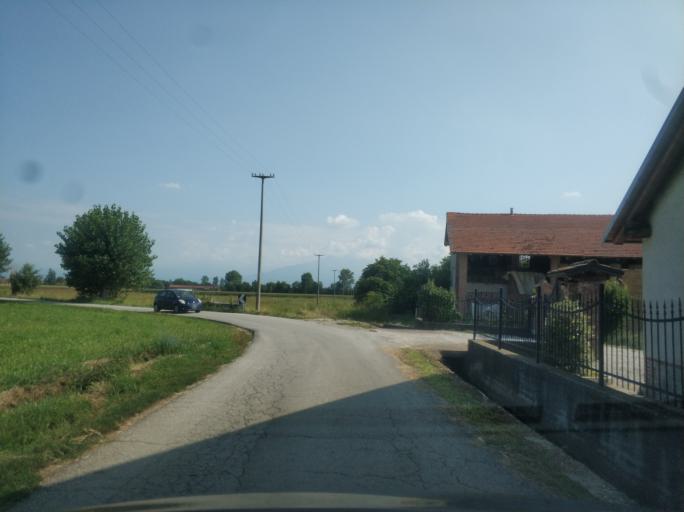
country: IT
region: Piedmont
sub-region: Provincia di Cuneo
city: Roata Rossi
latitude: 44.4545
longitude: 7.4736
